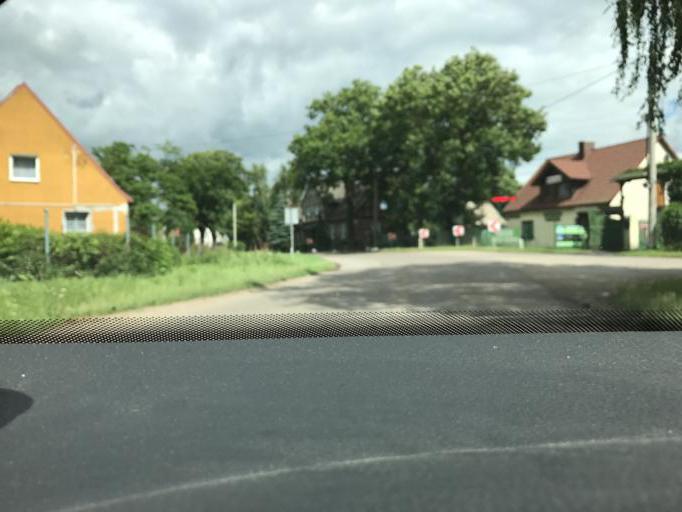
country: PL
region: Pomeranian Voivodeship
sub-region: Powiat gdanski
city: Pruszcz Gdanski
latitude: 54.2742
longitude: 18.6908
